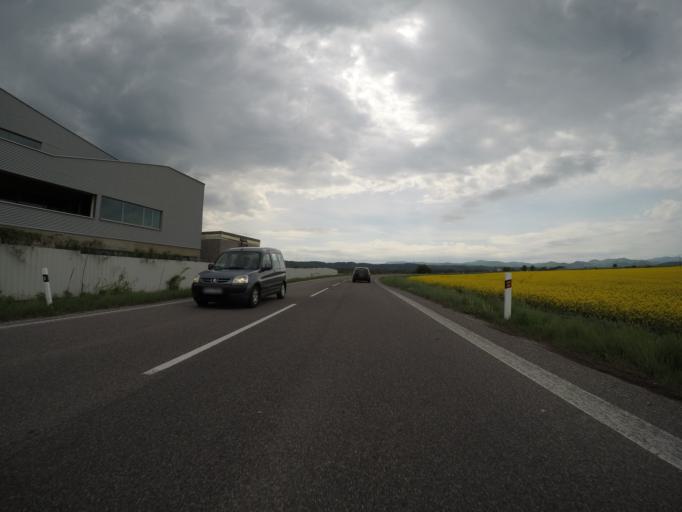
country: SK
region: Banskobystricky
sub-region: Okres Banska Bystrica
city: Zvolen
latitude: 48.6564
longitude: 19.1435
